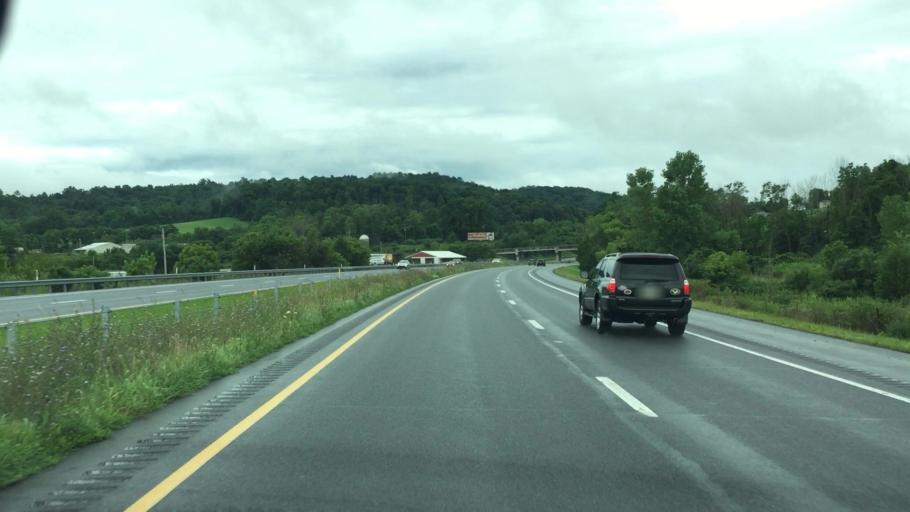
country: US
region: Maryland
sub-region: Washington County
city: Hancock
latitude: 39.7520
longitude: -78.1836
